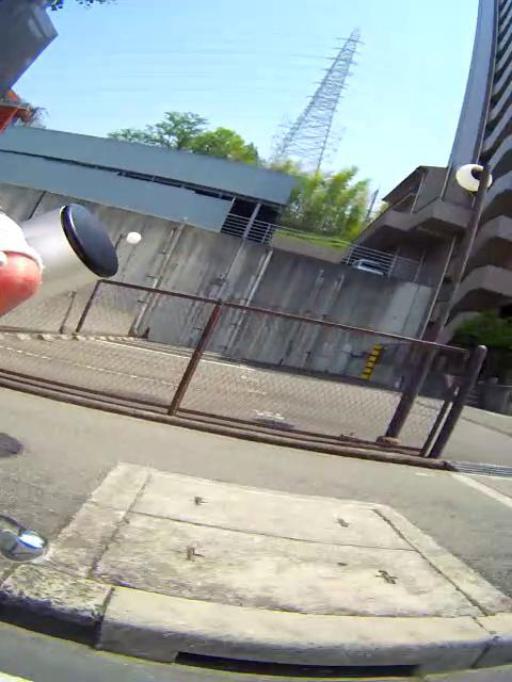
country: JP
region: Osaka
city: Suita
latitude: 34.7777
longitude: 135.4964
